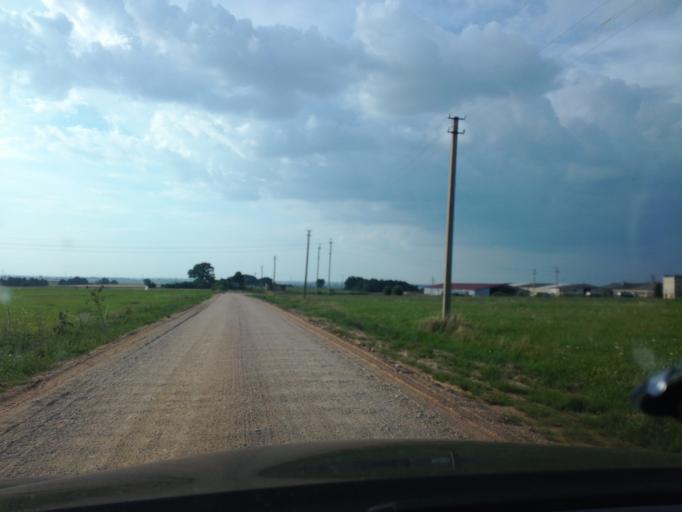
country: LT
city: Simnas
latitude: 54.3908
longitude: 23.8169
